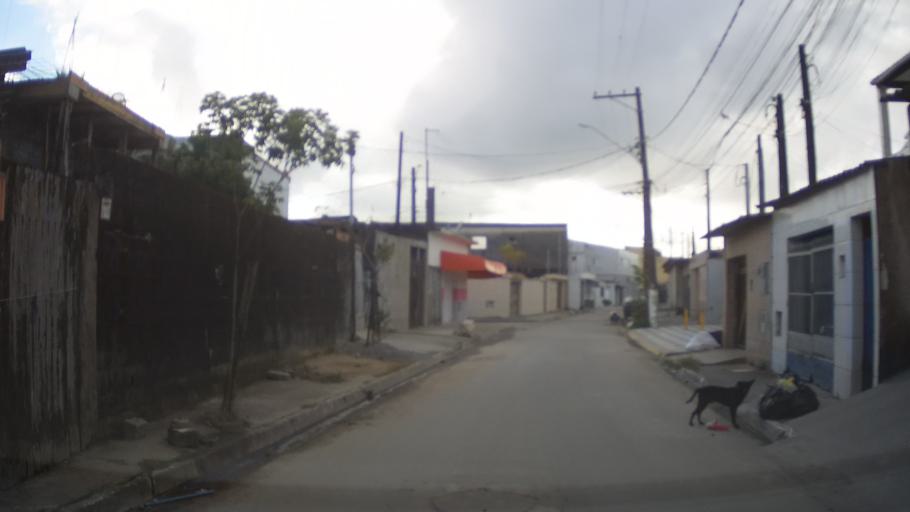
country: BR
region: Sao Paulo
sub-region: Praia Grande
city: Praia Grande
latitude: -24.0115
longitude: -46.4729
